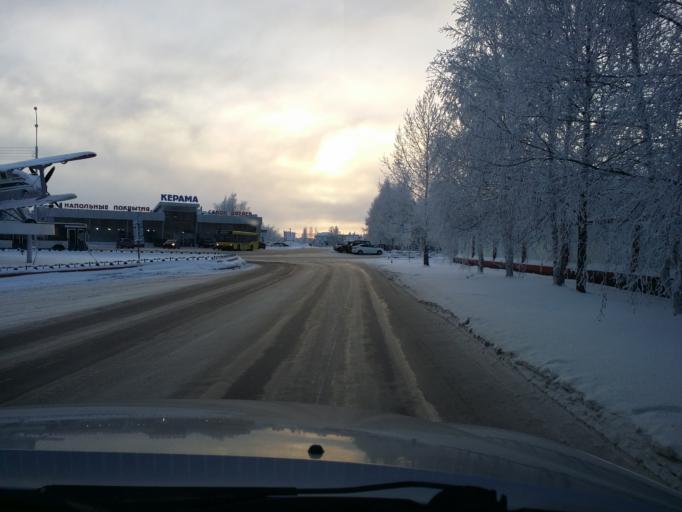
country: RU
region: Khanty-Mansiyskiy Avtonomnyy Okrug
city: Nizhnevartovsk
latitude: 60.9509
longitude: 76.5003
